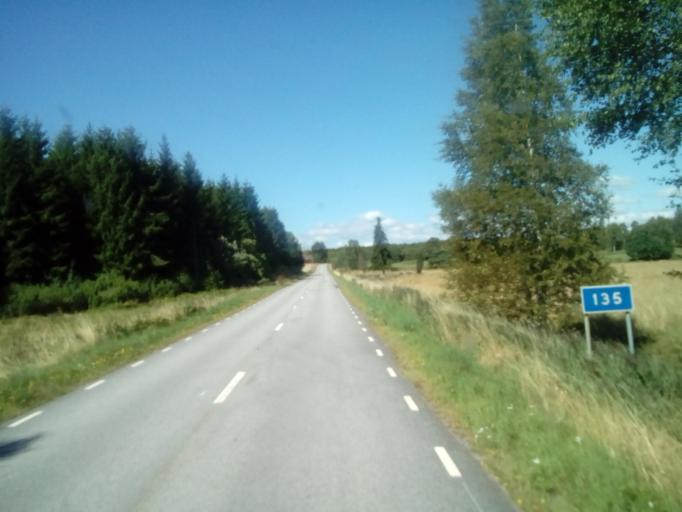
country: SE
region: Kalmar
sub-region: Vasterviks Kommun
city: Overum
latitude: 57.9009
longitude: 16.0551
